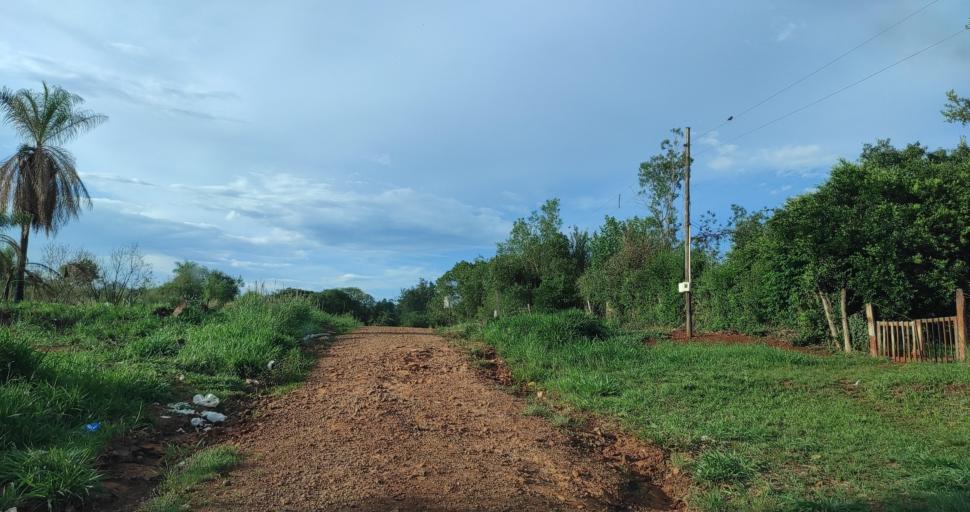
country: AR
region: Misiones
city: Santo Pipo
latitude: -27.1500
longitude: -55.4210
